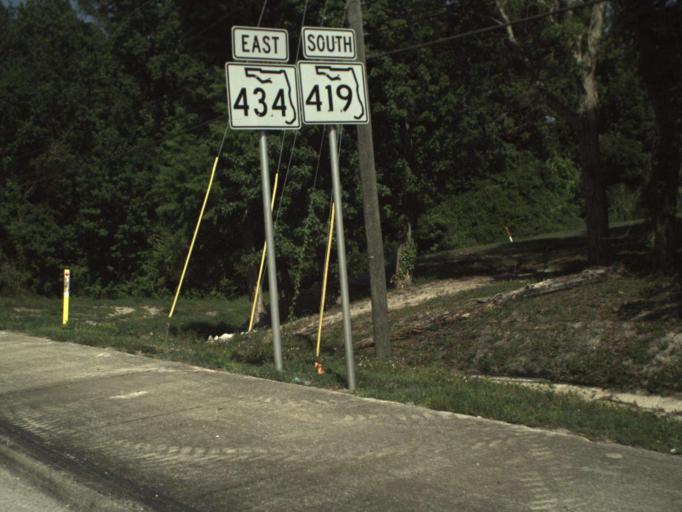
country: US
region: Florida
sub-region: Seminole County
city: Winter Springs
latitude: 28.7036
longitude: -81.2909
